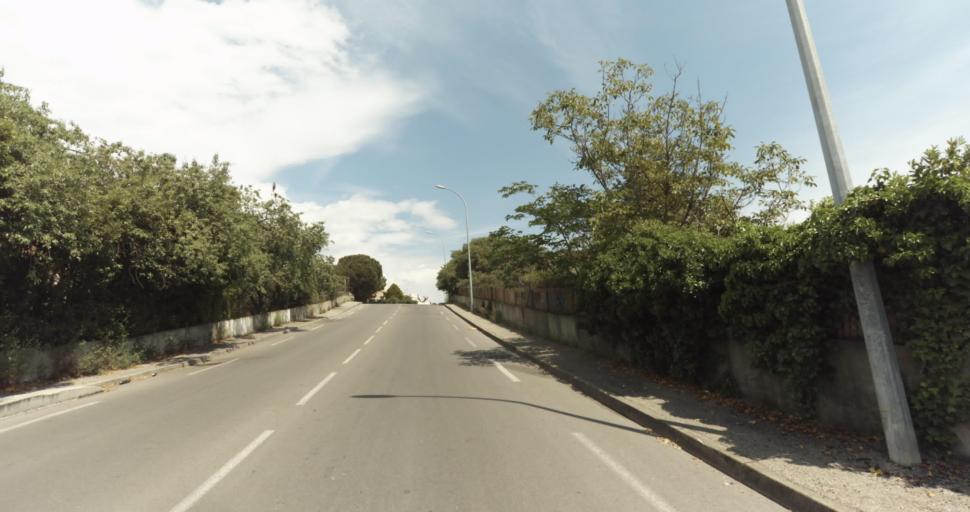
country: FR
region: Languedoc-Roussillon
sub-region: Departement du Gard
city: Nimes
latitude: 43.8465
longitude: 4.3807
